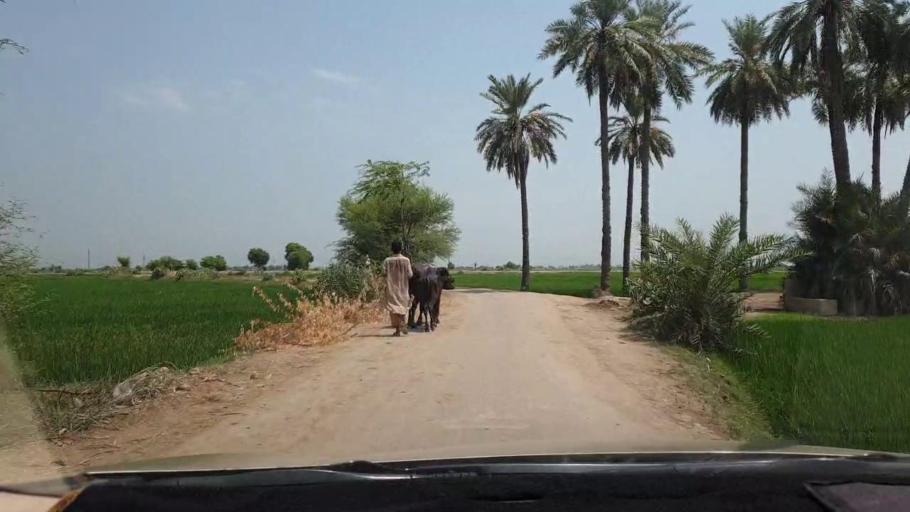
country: PK
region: Sindh
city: Naudero
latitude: 27.6581
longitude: 68.3247
